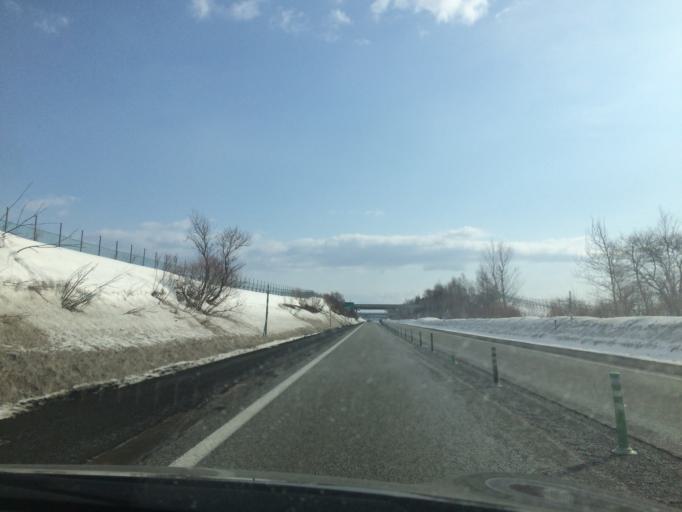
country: JP
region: Hokkaido
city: Chitose
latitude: 42.8931
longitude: 141.7986
